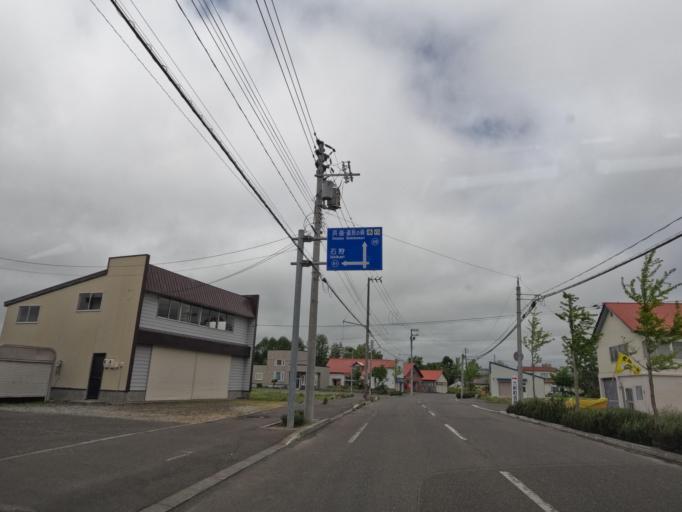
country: JP
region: Hokkaido
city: Tobetsu
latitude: 43.2371
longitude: 141.5134
